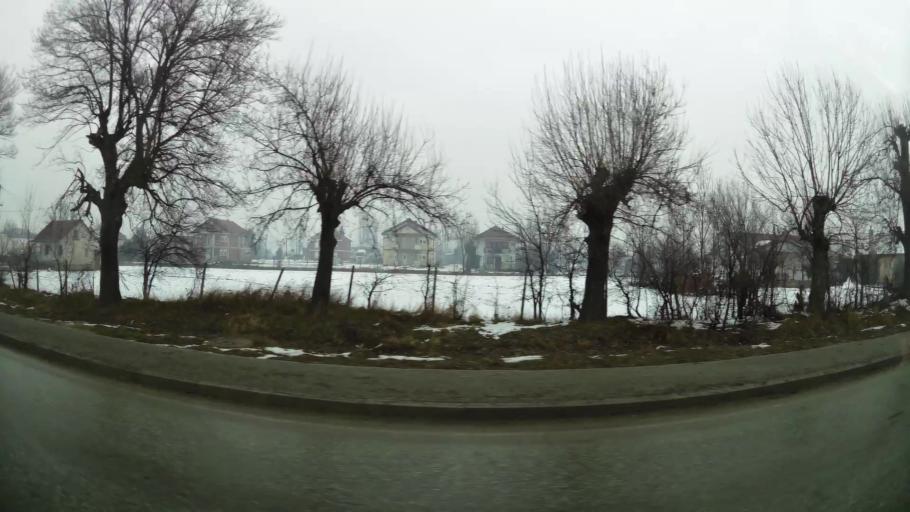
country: MK
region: Petrovec
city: Petrovec
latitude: 41.9307
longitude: 21.6252
